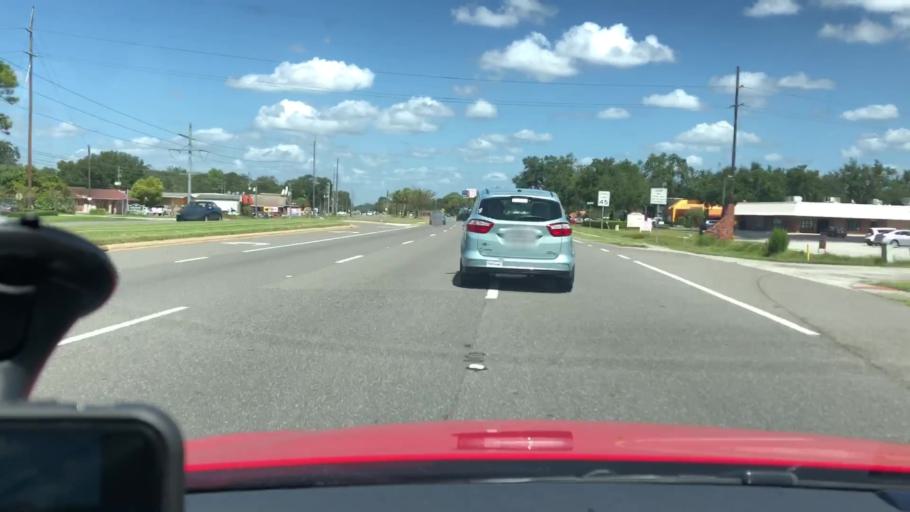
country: US
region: Florida
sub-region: Volusia County
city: Orange City
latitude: 28.9242
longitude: -81.2991
